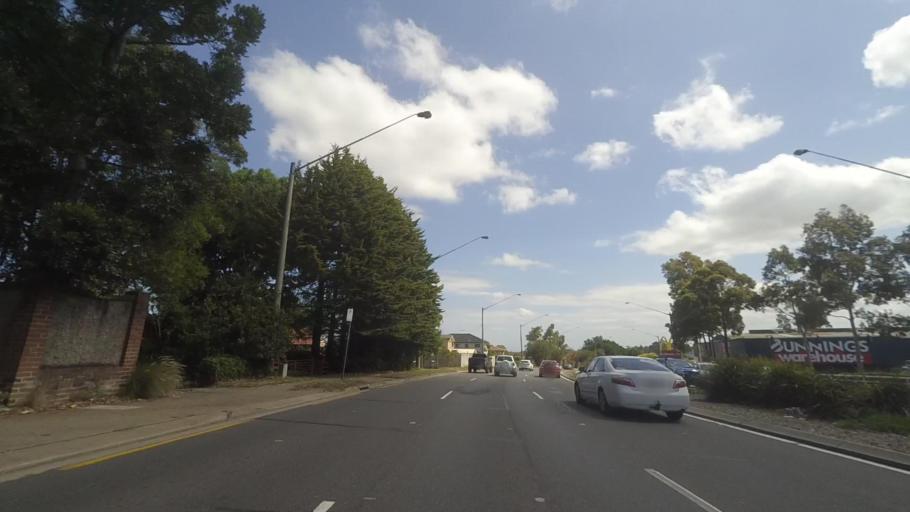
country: AU
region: New South Wales
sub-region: Hornsby Shire
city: Pennant Hills
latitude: -33.7288
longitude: 151.0840
